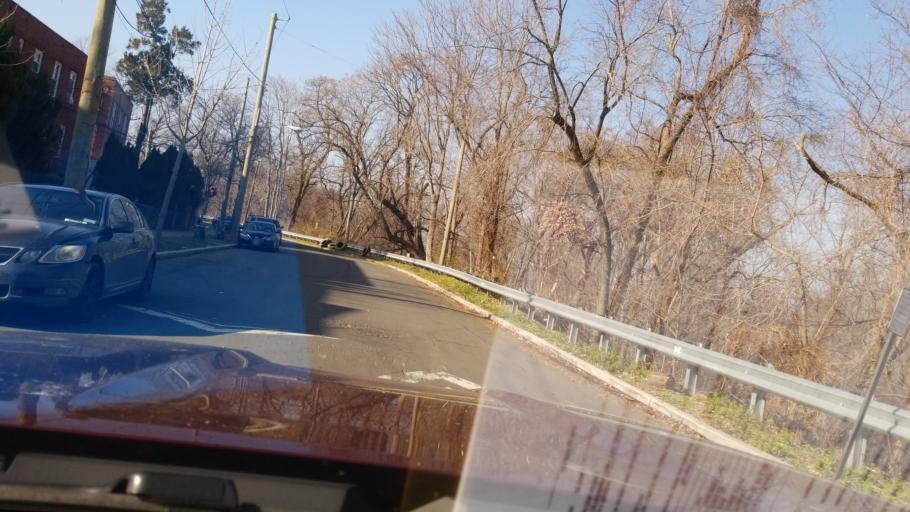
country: US
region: Maryland
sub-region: Prince George's County
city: Glassmanor
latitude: 38.8485
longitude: -77.0005
